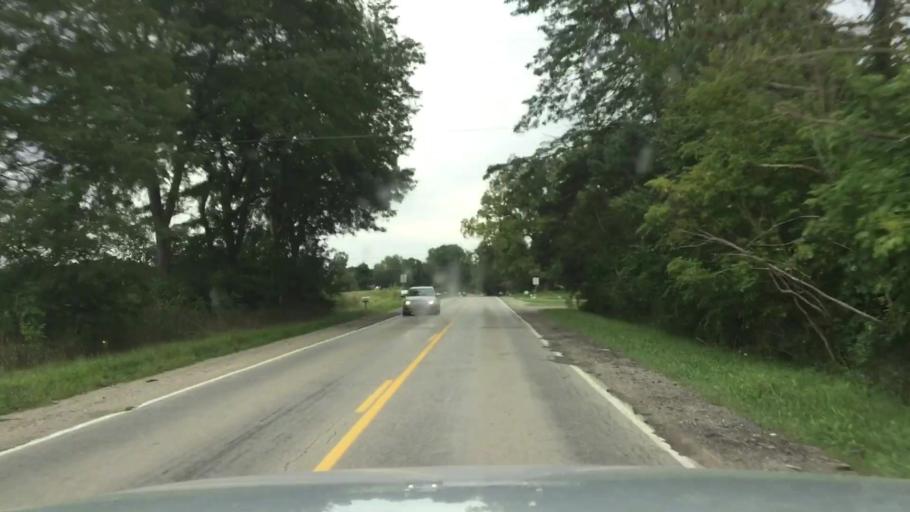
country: US
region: Michigan
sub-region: Genesee County
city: Argentine
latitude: 42.8023
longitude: -83.8705
